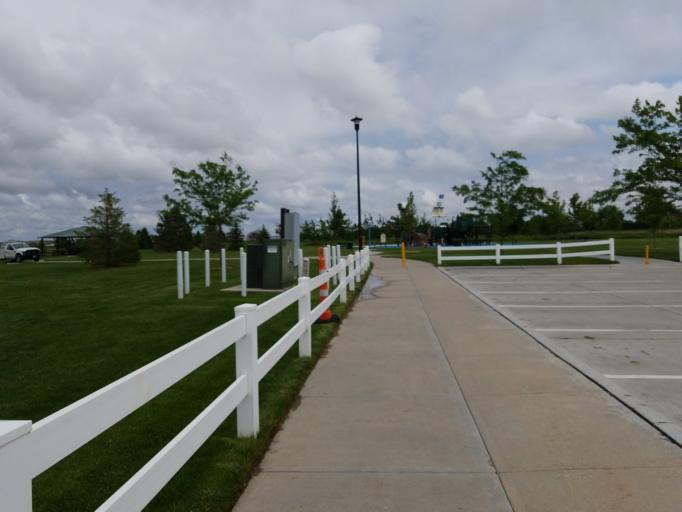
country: US
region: Nebraska
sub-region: Buffalo County
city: Kearney
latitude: 40.6799
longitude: -99.1083
